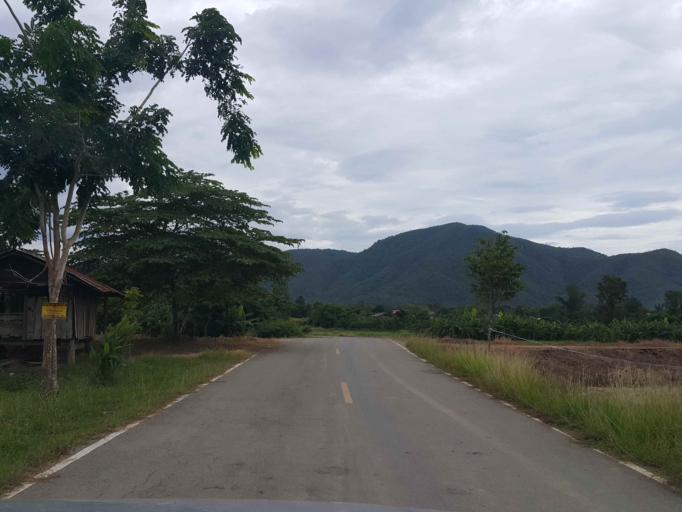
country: TH
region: Sukhothai
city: Thung Saliam
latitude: 17.3391
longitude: 99.4402
